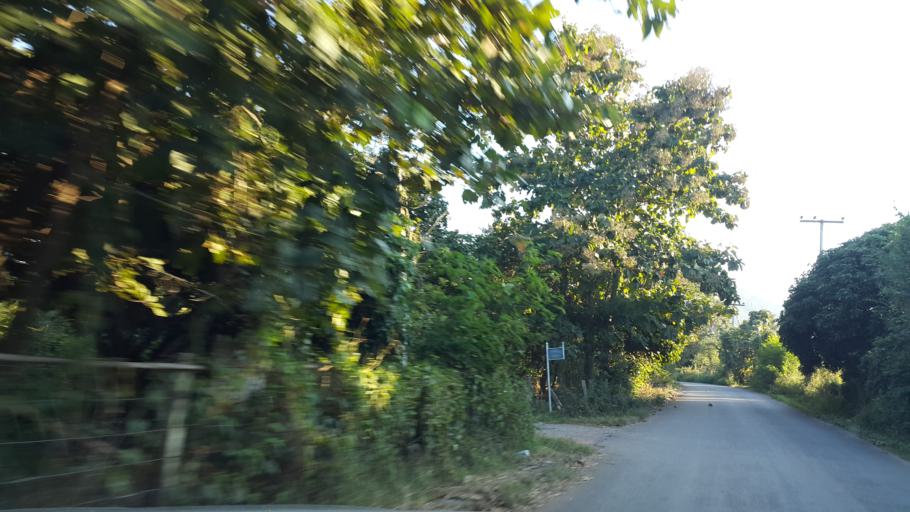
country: TH
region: Chiang Mai
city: Mae On
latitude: 18.7288
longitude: 99.2259
